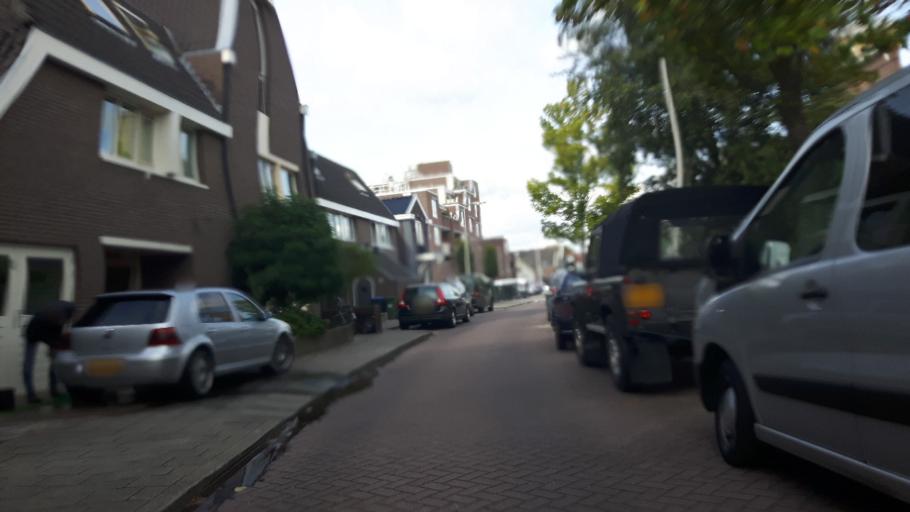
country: NL
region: South Holland
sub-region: Bodegraven-Reeuwijk
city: Bodegraven
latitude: 52.0866
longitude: 4.7423
